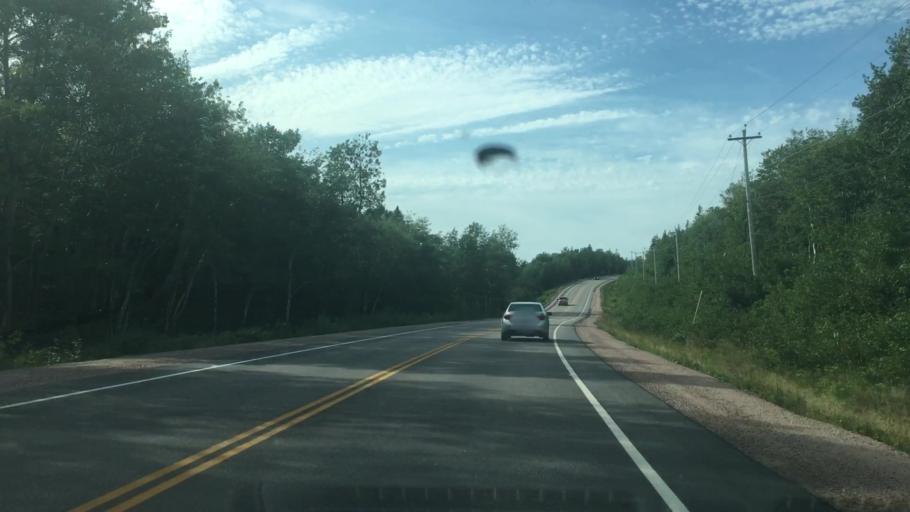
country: CA
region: Nova Scotia
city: Sydney Mines
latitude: 46.8207
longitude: -60.3545
